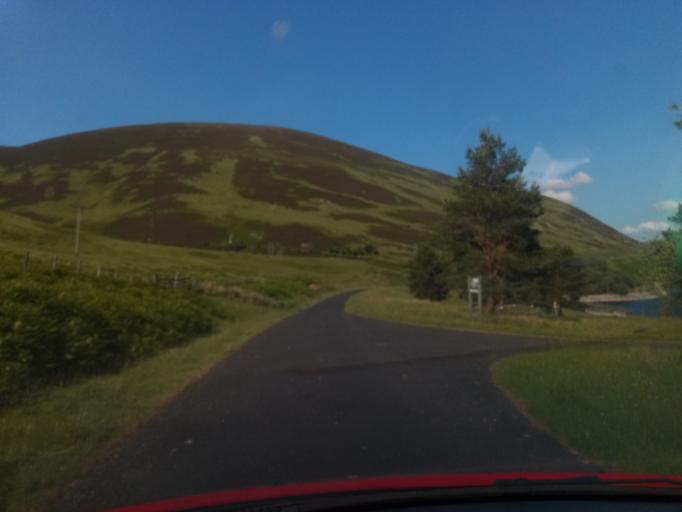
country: GB
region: Scotland
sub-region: The Scottish Borders
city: Peebles
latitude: 55.4840
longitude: -3.3018
